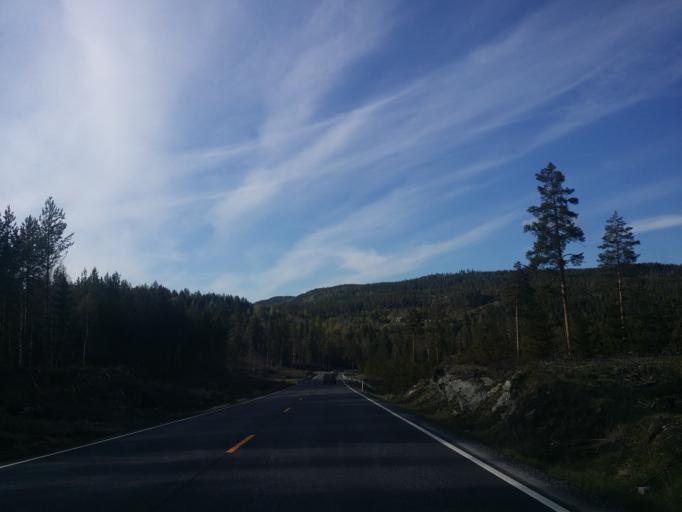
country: NO
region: Buskerud
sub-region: Kongsberg
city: Kongsberg
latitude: 59.6218
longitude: 9.4740
